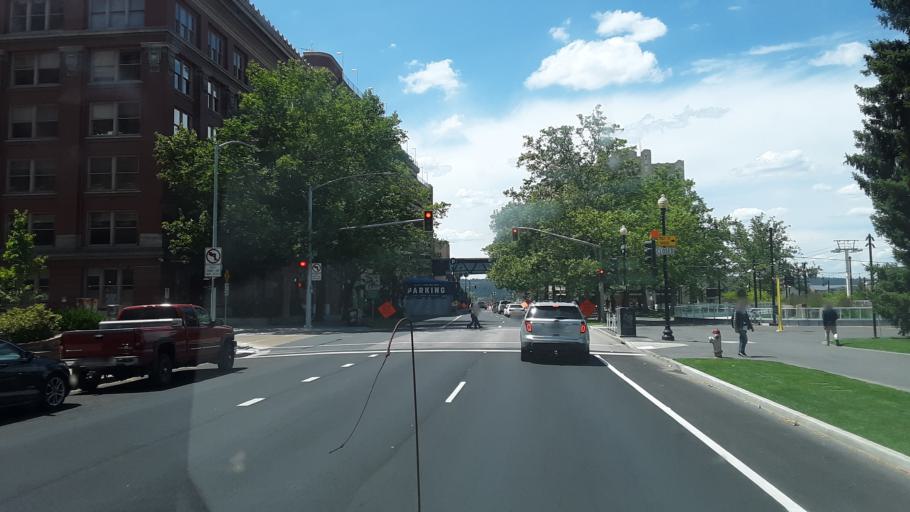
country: US
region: Washington
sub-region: Spokane County
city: Spokane
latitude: 47.6602
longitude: -117.4217
